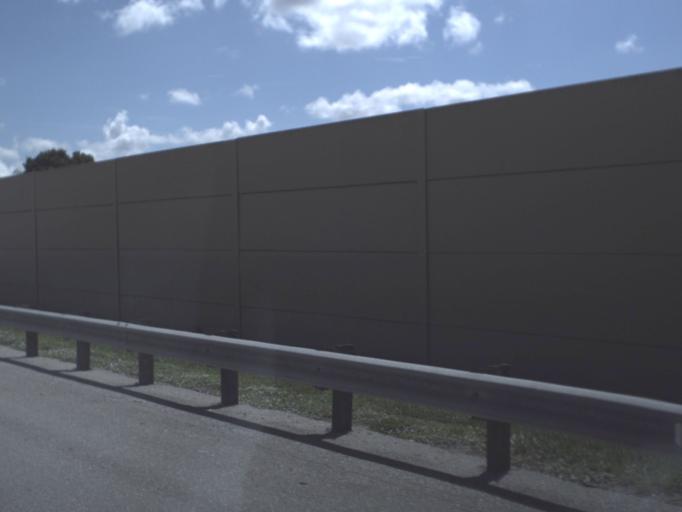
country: US
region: Florida
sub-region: Lee County
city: Lochmoor Waterway Estates
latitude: 26.6076
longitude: -81.9259
